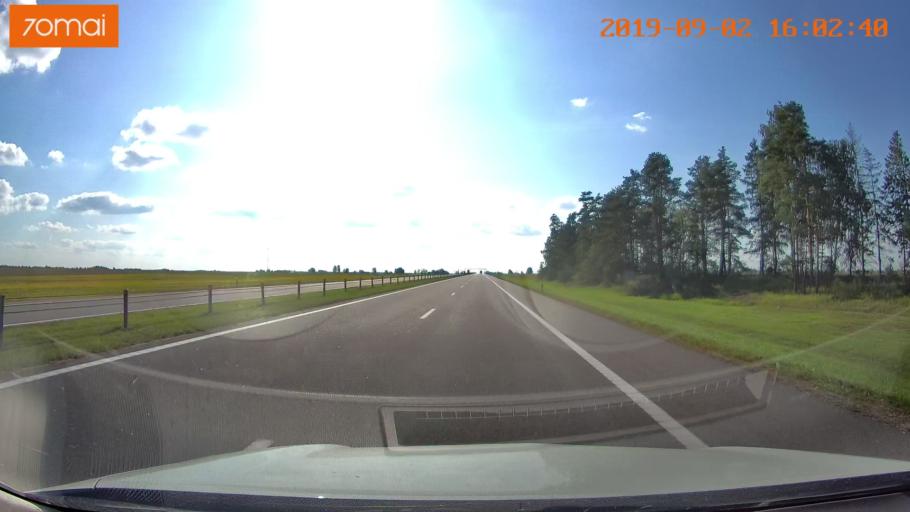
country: BY
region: Minsk
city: Byerazino
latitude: 53.8089
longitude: 28.8908
